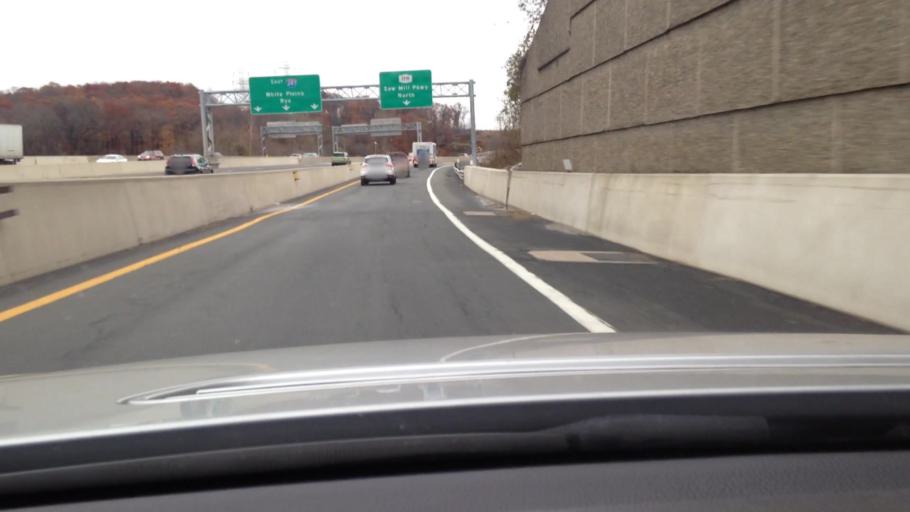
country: US
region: New York
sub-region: Westchester County
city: Elmsford
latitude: 41.0585
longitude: -73.8305
